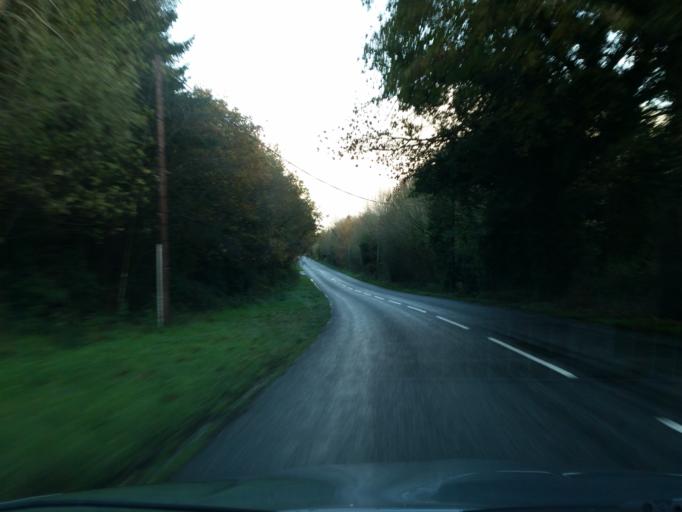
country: GB
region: Northern Ireland
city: Lisnaskea
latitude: 54.2085
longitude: -7.4805
